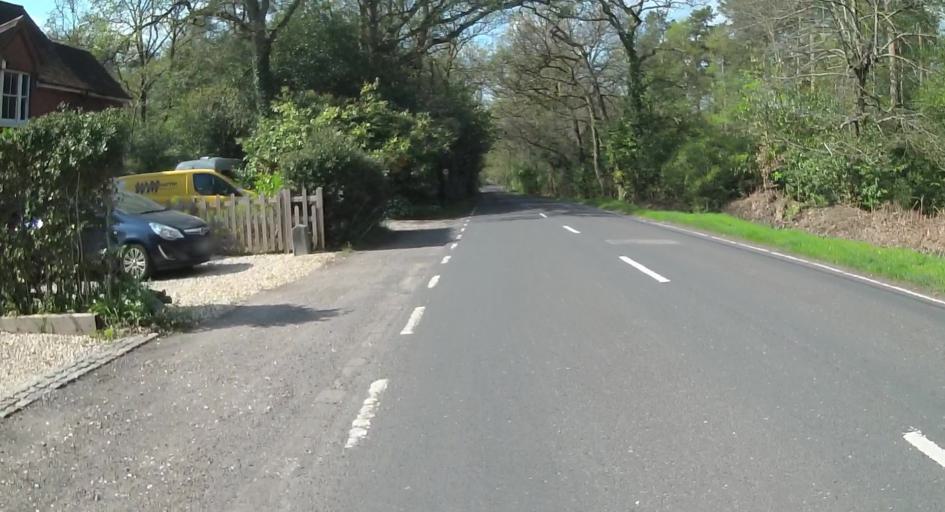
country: GB
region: England
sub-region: Hampshire
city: Tadley
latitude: 51.3598
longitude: -1.1091
